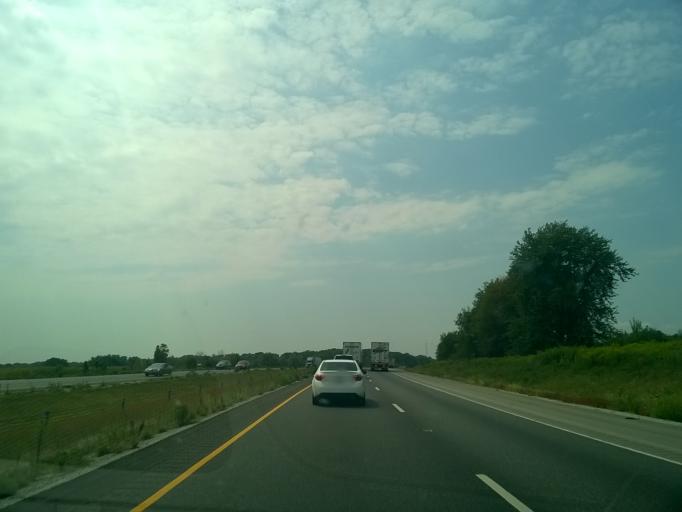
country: US
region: Indiana
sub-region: Clay County
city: Brazil
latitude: 39.4695
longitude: -87.0339
